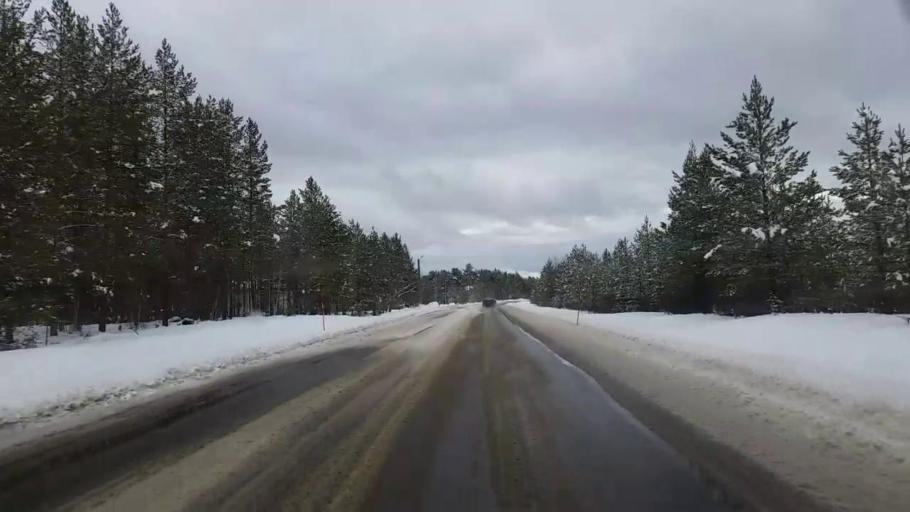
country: SE
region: Vaesternorrland
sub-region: Ange Kommun
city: Ange
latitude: 62.0434
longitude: 15.1812
